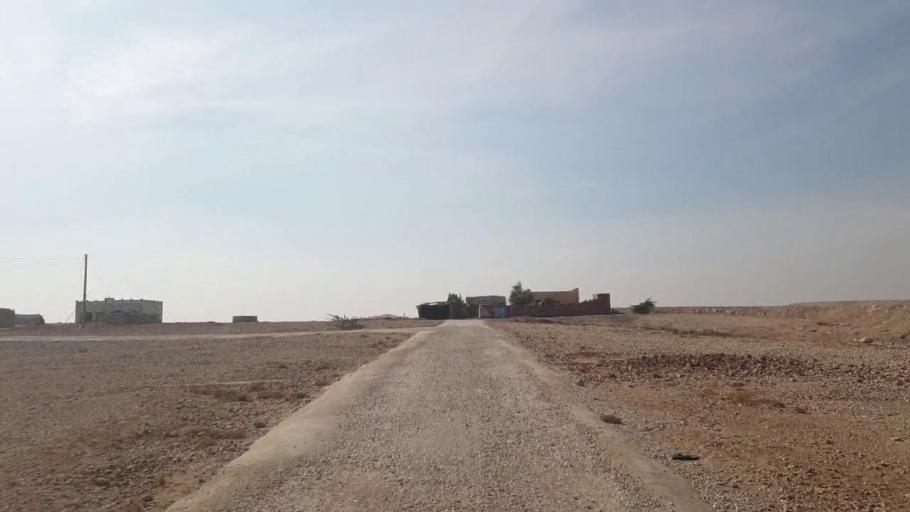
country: PK
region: Sindh
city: Hala
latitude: 25.7807
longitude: 68.2761
